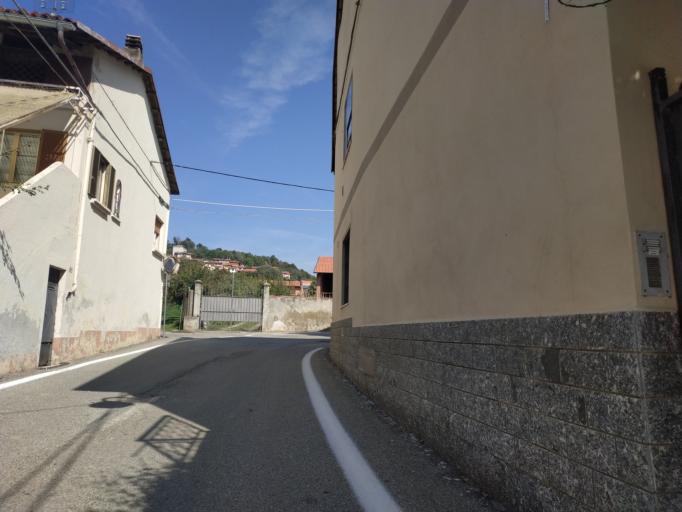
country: IT
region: Piedmont
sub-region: Provincia di Torino
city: Orio Canavese
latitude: 45.3262
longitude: 7.8601
